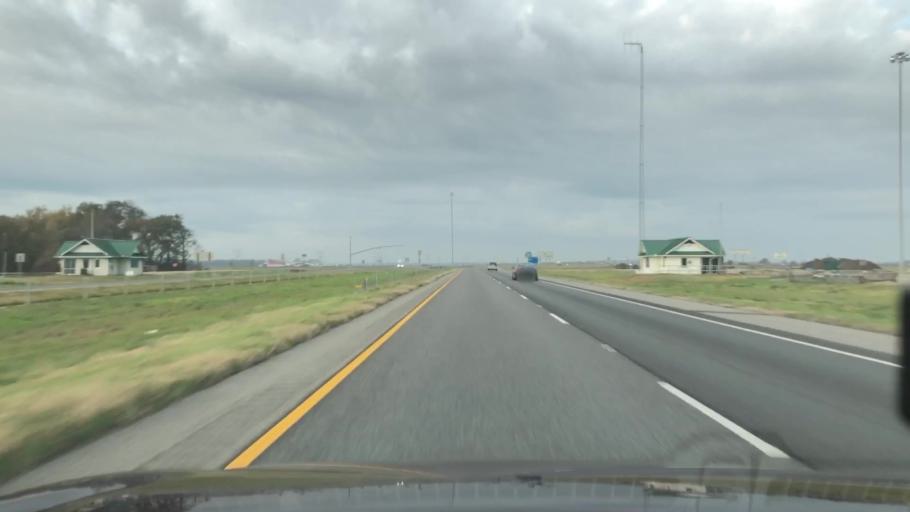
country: US
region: Mississippi
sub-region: Warren County
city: Vicksburg
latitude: 32.3202
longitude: -90.9468
